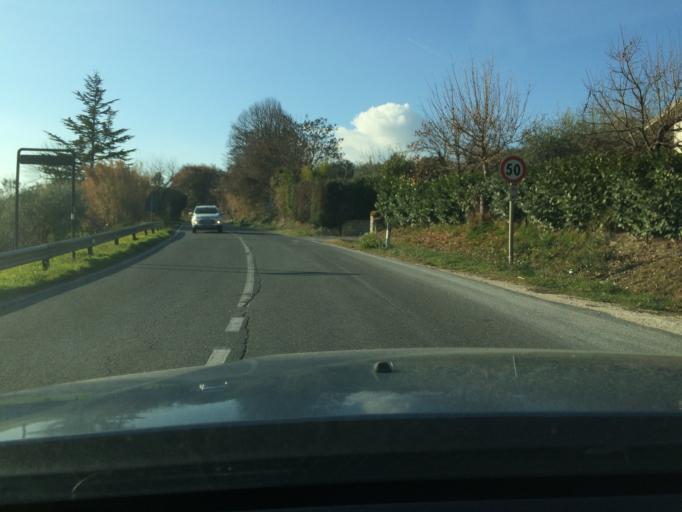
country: IT
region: Umbria
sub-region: Provincia di Terni
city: Amelia
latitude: 42.5583
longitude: 12.4373
